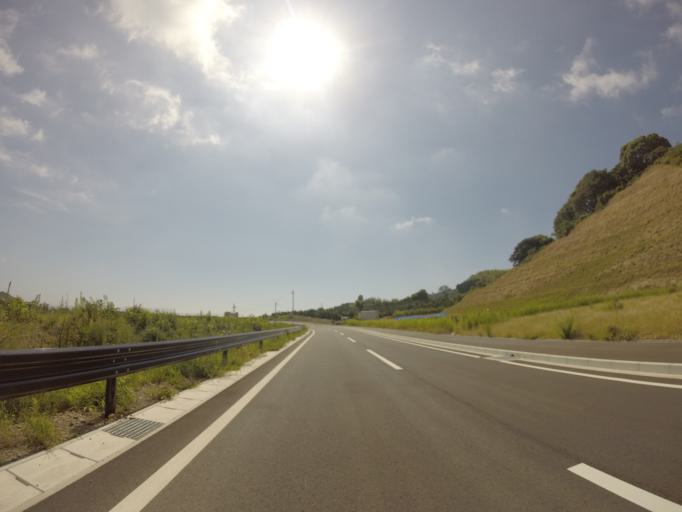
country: JP
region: Shizuoka
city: Shizuoka-shi
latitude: 34.9866
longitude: 138.4707
